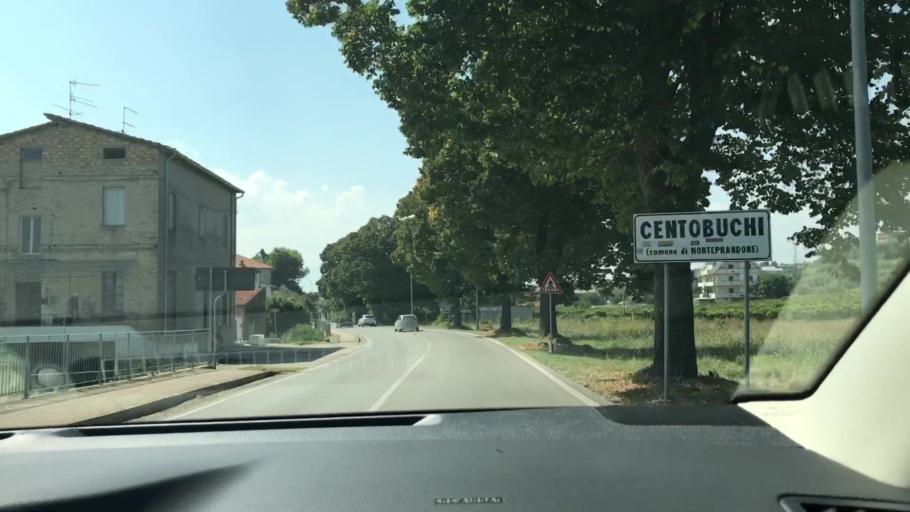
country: IT
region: The Marches
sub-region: Provincia di Ascoli Piceno
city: San Benedetto del Tronto
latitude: 42.9061
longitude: 13.8684
